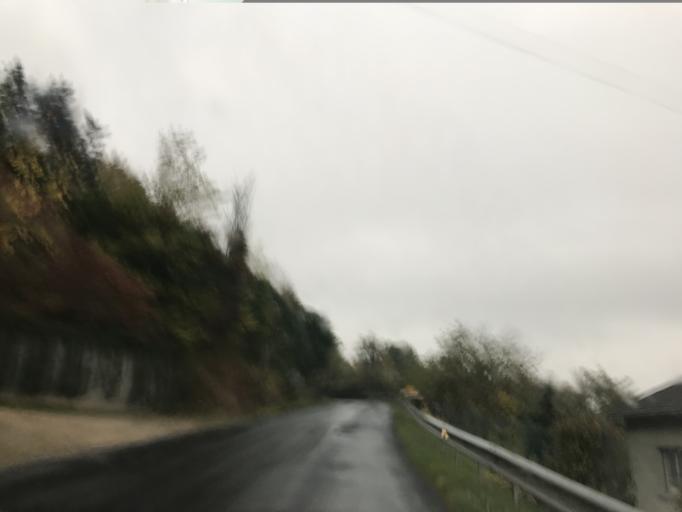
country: FR
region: Auvergne
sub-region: Departement du Puy-de-Dome
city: Courpiere
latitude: 45.7556
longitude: 3.5527
